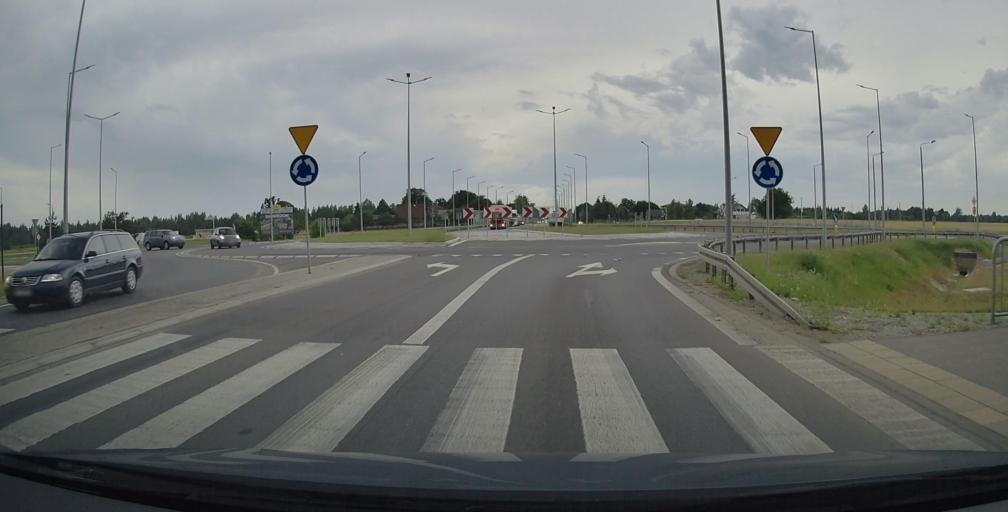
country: PL
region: Lublin Voivodeship
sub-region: Biala Podlaska
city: Biala Podlaska
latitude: 52.0398
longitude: 23.1880
